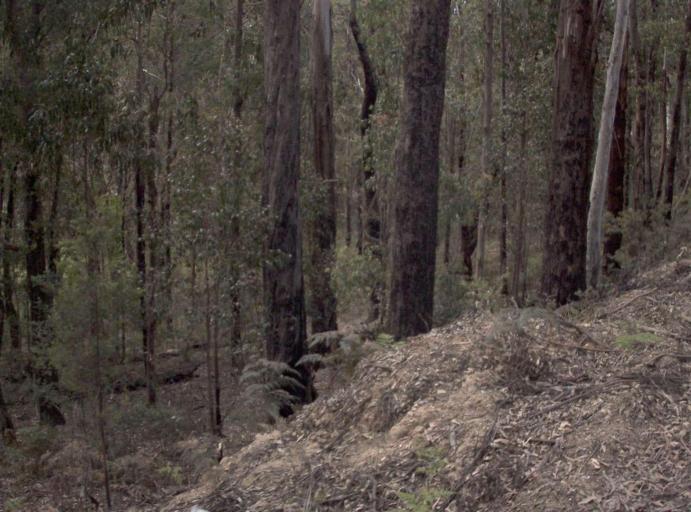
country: AU
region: New South Wales
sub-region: Bombala
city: Bombala
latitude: -37.1867
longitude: 148.7063
